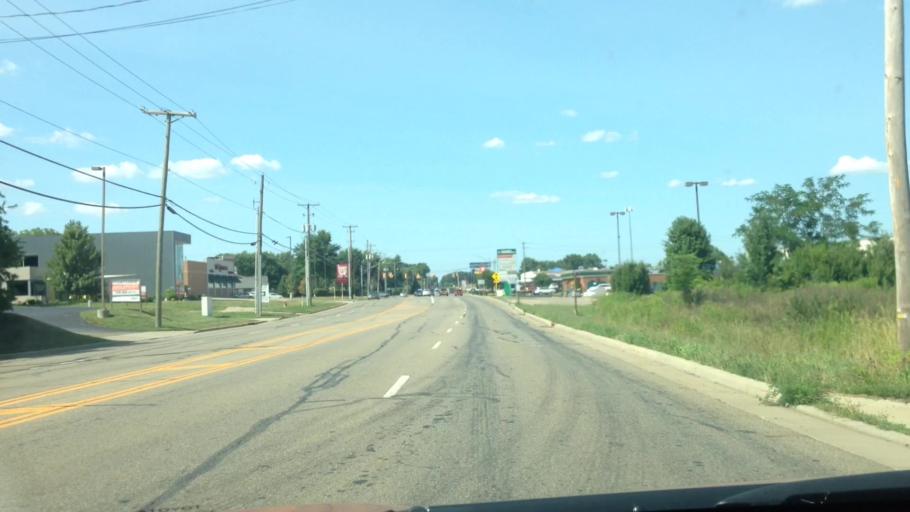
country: US
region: Ohio
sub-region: Stark County
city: North Canton
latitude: 40.8768
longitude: -81.4413
